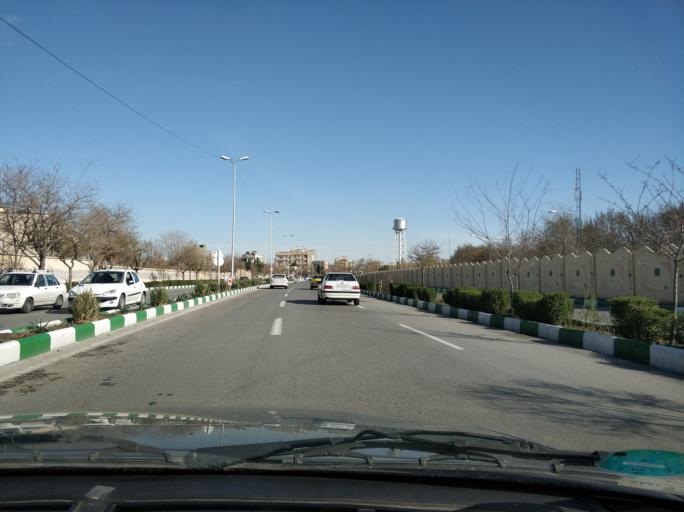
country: IR
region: Razavi Khorasan
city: Mashhad
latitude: 36.3028
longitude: 59.6294
